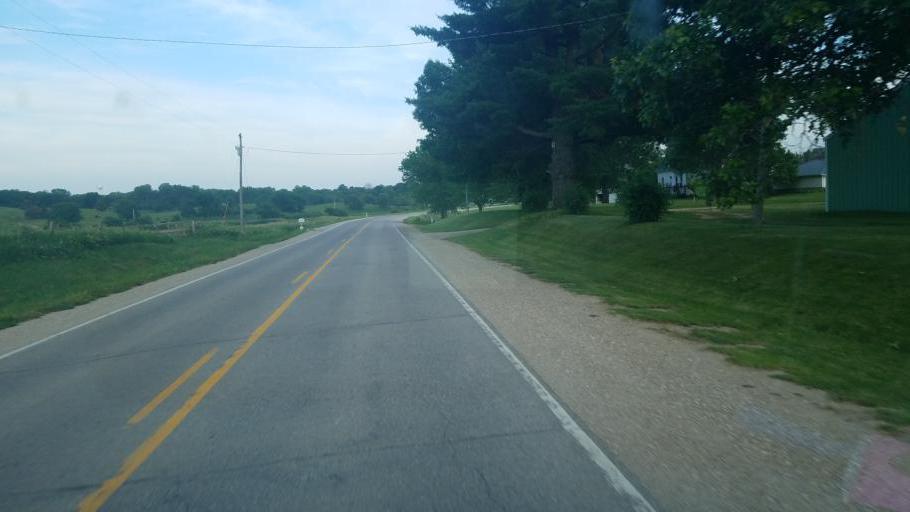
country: US
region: Iowa
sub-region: Benton County
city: Belle Plaine
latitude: 41.9354
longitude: -92.4033
